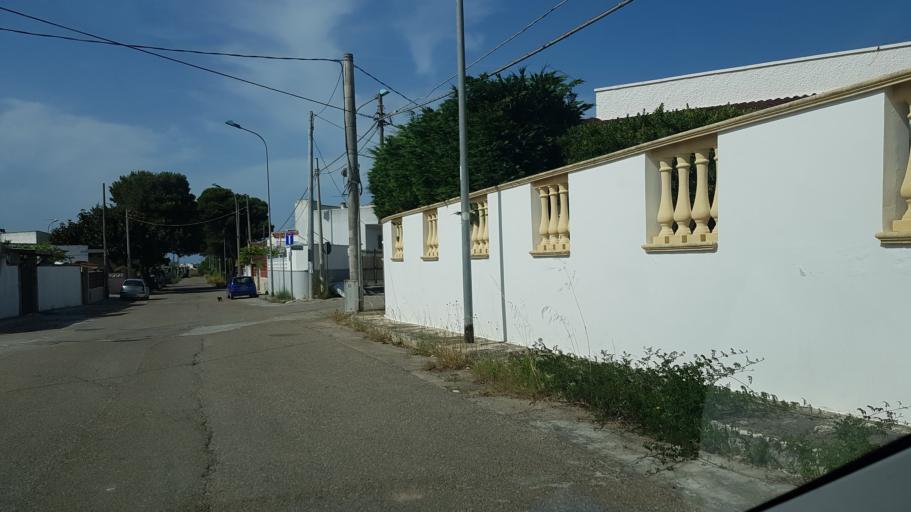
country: IT
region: Apulia
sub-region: Provincia di Brindisi
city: Torchiarolo
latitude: 40.5268
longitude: 18.0754
